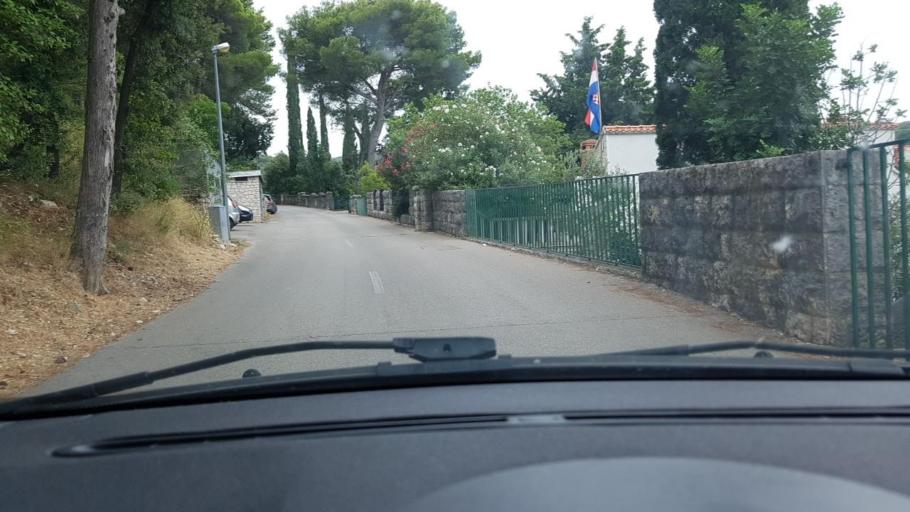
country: HR
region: Dubrovacko-Neretvanska
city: Korcula
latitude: 42.9619
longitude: 17.1281
